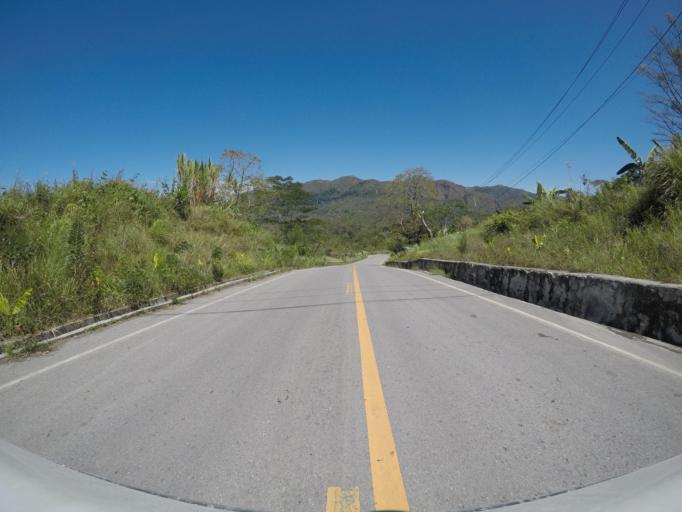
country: TL
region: Manatuto
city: Manatuto
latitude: -8.7768
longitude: 125.9675
